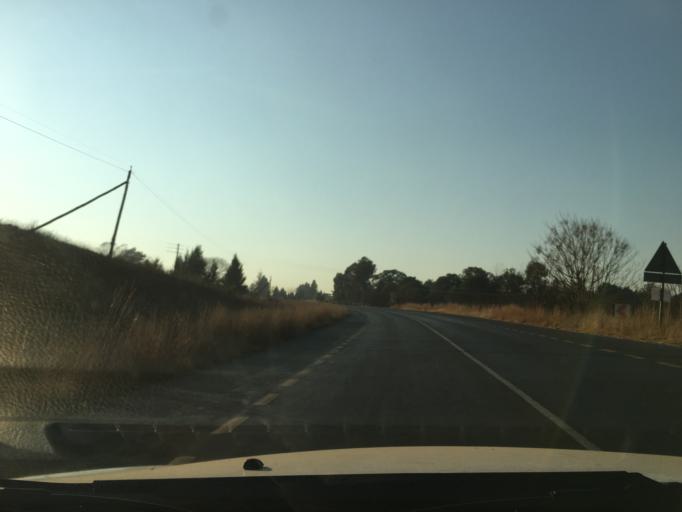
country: ZA
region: Gauteng
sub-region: West Rand District Municipality
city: Muldersdriseloop
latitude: -25.9925
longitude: 27.8482
